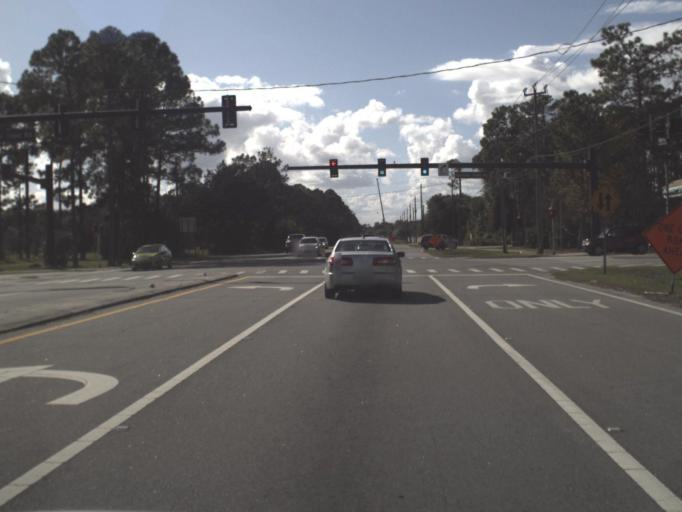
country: US
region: Florida
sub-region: Volusia County
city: Port Orange
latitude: 29.1035
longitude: -81.0350
